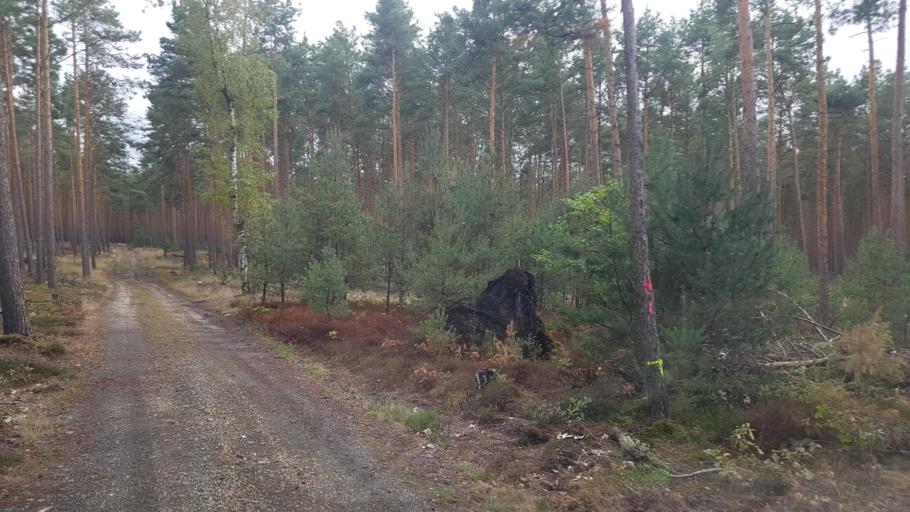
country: DE
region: Brandenburg
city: Elsterwerda
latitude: 51.4908
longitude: 13.4601
